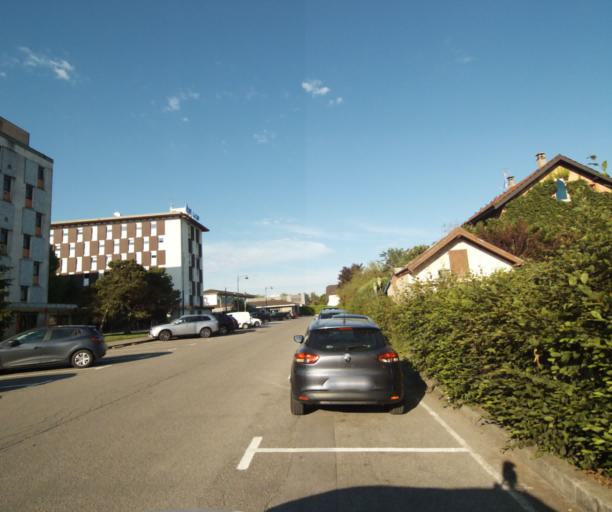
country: FR
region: Rhone-Alpes
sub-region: Departement de la Haute-Savoie
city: Thonon-les-Bains
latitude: 46.3636
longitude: 6.4662
